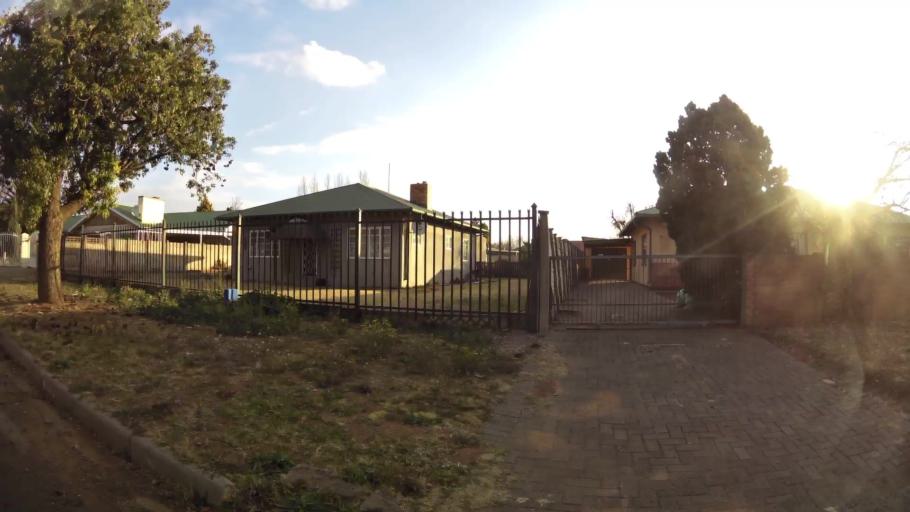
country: ZA
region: Orange Free State
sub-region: Mangaung Metropolitan Municipality
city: Bloemfontein
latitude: -29.1370
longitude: 26.1960
